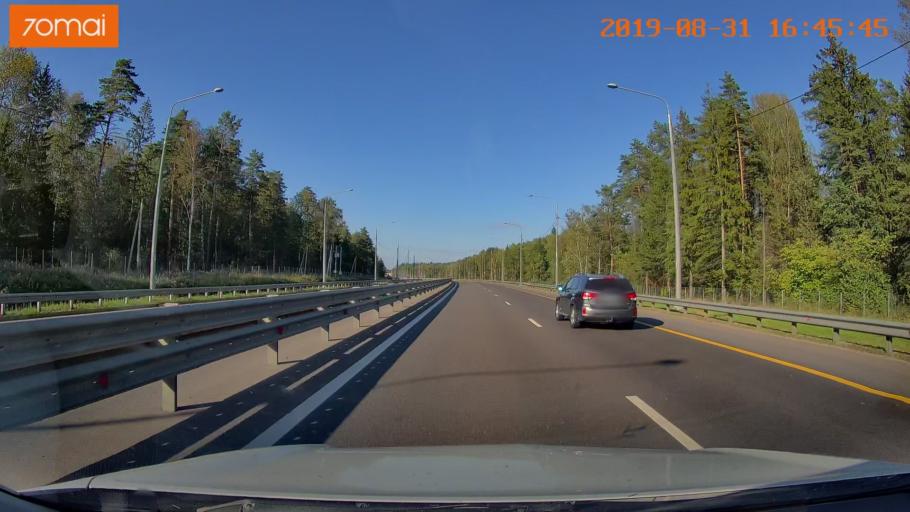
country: RU
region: Kaluga
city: Mstikhino
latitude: 54.6240
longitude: 36.1230
